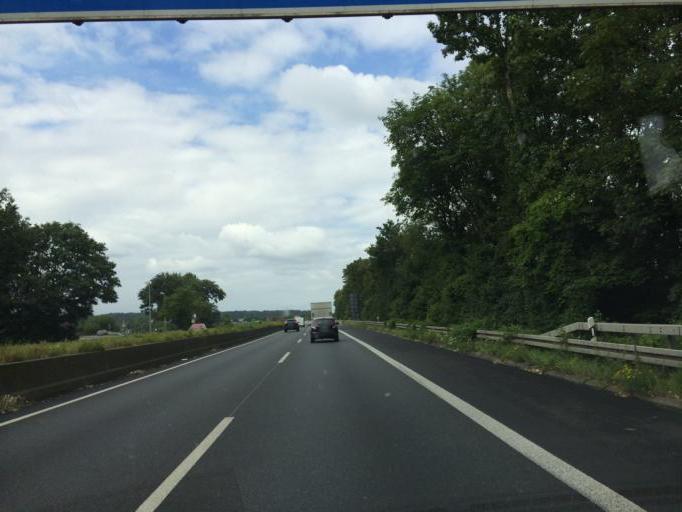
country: DE
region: North Rhine-Westphalia
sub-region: Regierungsbezirk Dusseldorf
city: Muelheim (Ruhr)
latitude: 51.4463
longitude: 6.8331
